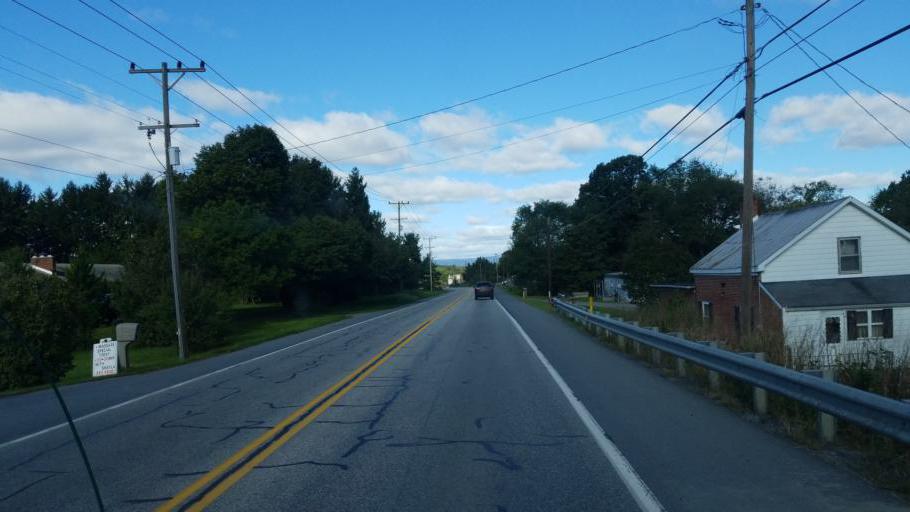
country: US
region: Pennsylvania
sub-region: Franklin County
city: Greencastle
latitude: 39.7956
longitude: -77.7652
